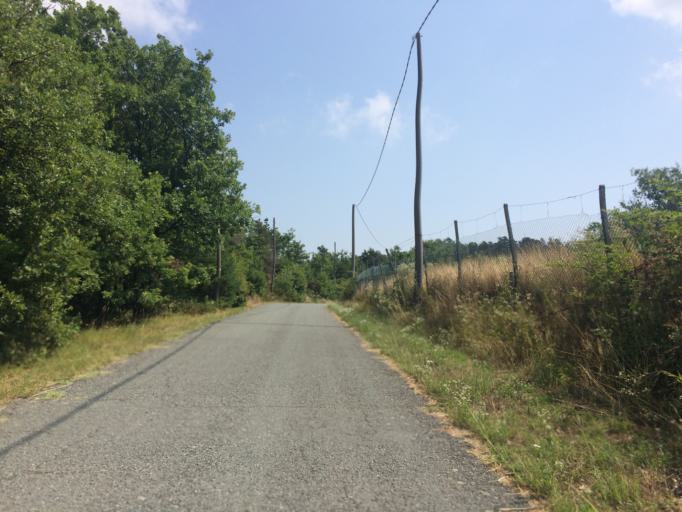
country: IT
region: Piedmont
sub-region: Provincia di Alessandria
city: Pareto
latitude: 44.5022
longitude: 8.3730
